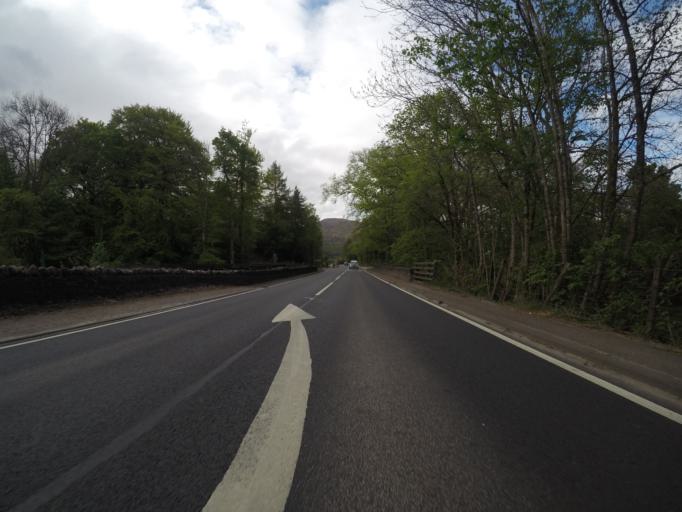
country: GB
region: Scotland
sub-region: Highland
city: Fort William
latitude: 56.8475
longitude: -5.0466
